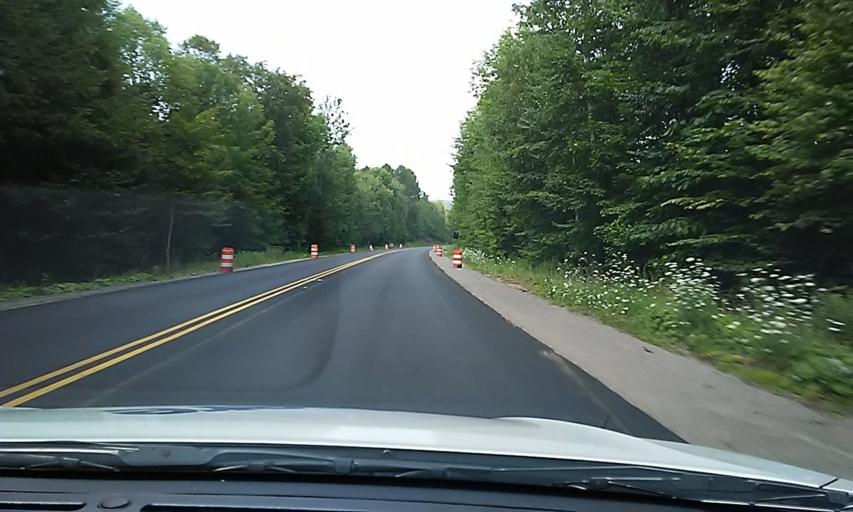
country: US
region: Pennsylvania
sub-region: Cameron County
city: Emporium
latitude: 41.6663
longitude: -78.1907
